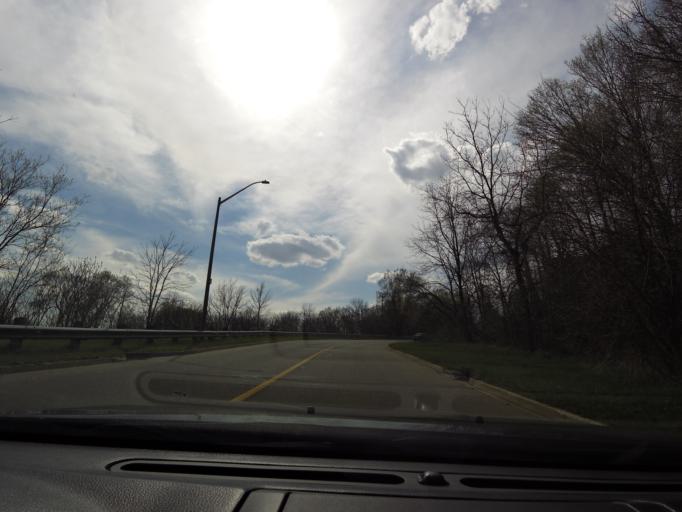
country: CA
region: Ontario
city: Cambridge
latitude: 43.3911
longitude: -80.3762
